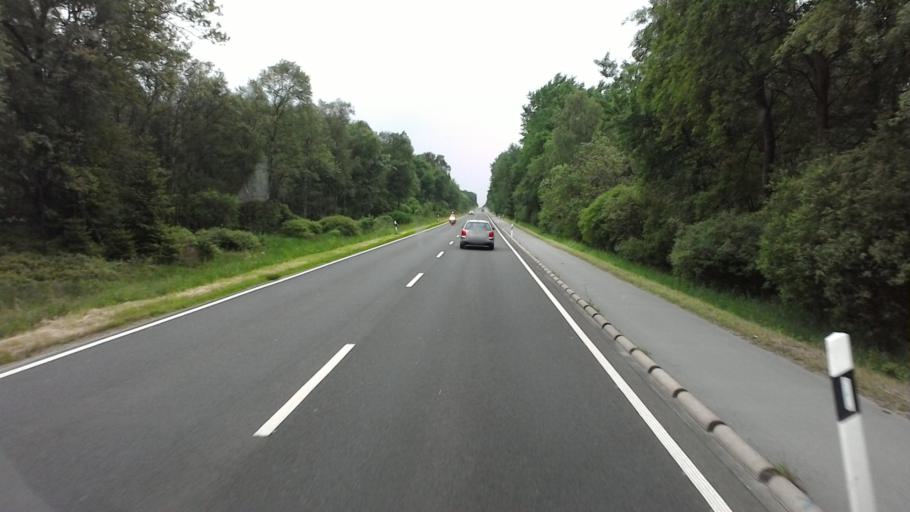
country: DE
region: North Rhine-Westphalia
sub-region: Regierungsbezirk Koln
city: Roetgen
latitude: 50.6200
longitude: 6.2391
